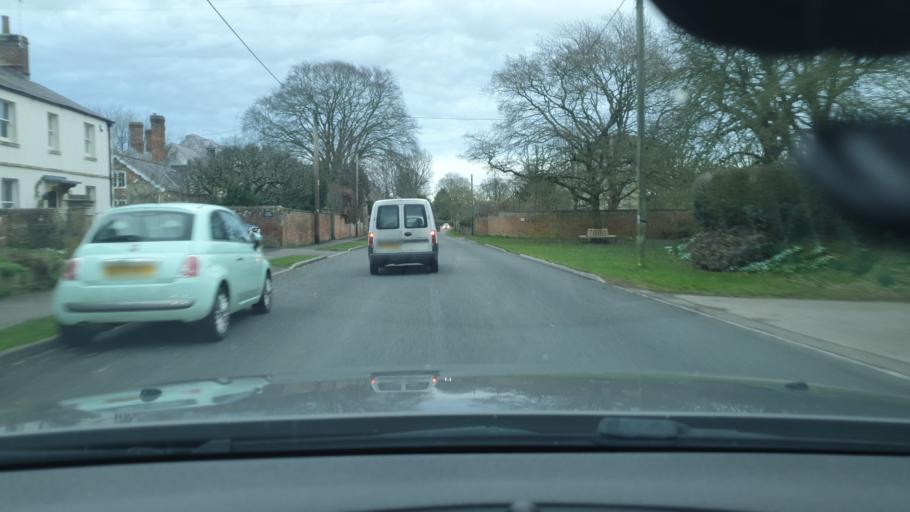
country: GB
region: England
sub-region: Wiltshire
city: Seend
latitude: 51.3492
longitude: -2.0789
